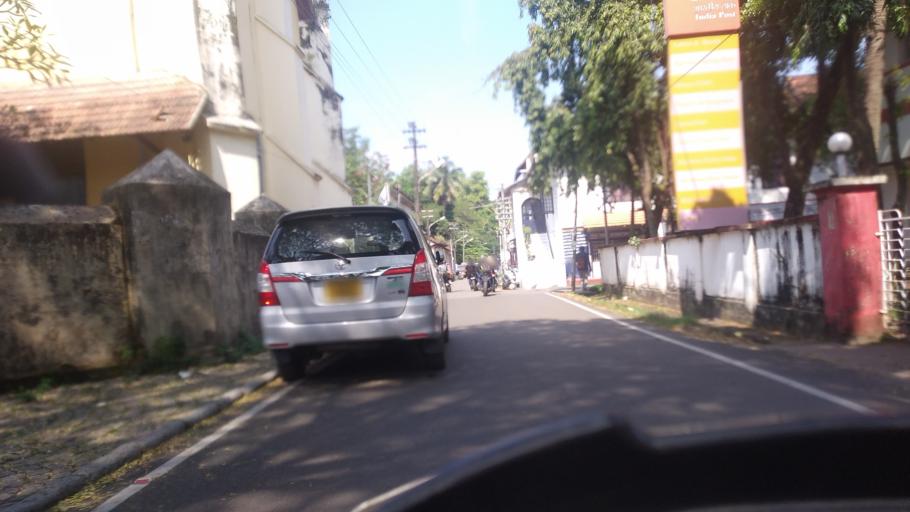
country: IN
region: Kerala
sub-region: Ernakulam
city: Cochin
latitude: 9.9657
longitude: 76.2413
